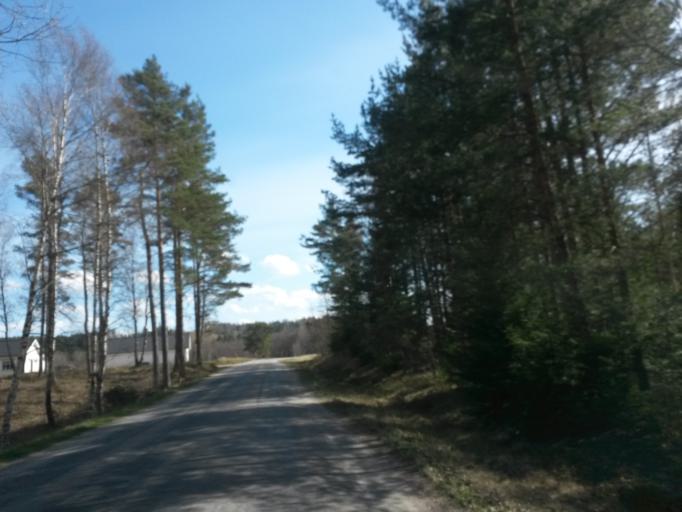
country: SE
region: Vaestra Goetaland
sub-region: Vargarda Kommun
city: Jonstorp
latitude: 57.9602
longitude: 12.7312
